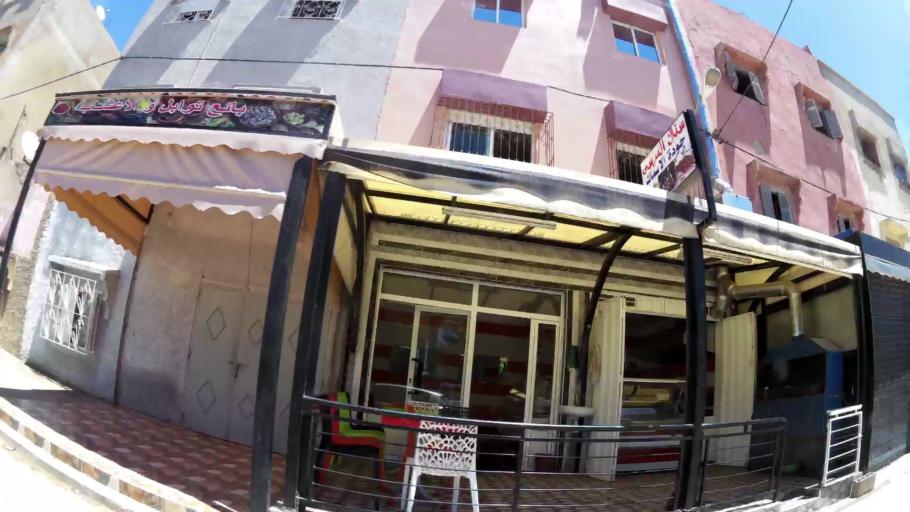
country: MA
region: Meknes-Tafilalet
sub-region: Meknes
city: Meknes
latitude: 33.9075
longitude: -5.5589
